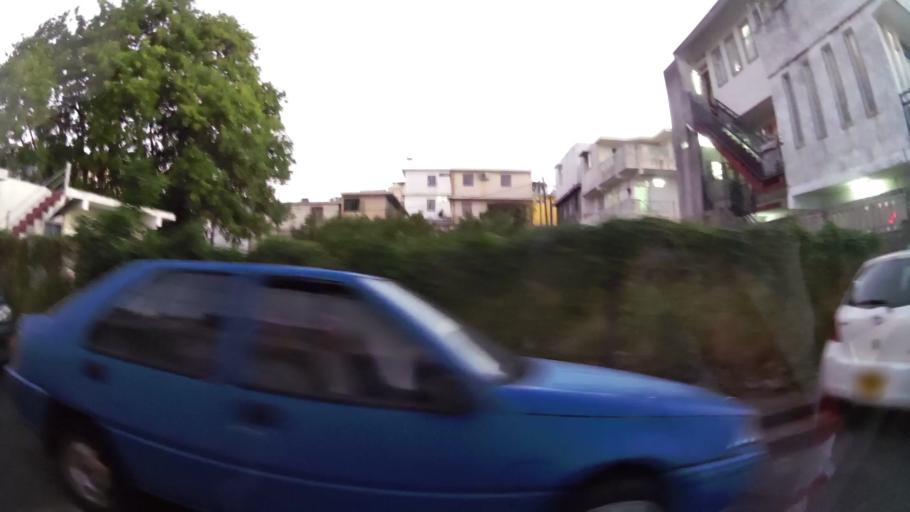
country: MU
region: Port Louis
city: Port Louis
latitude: -20.1661
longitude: 57.5145
